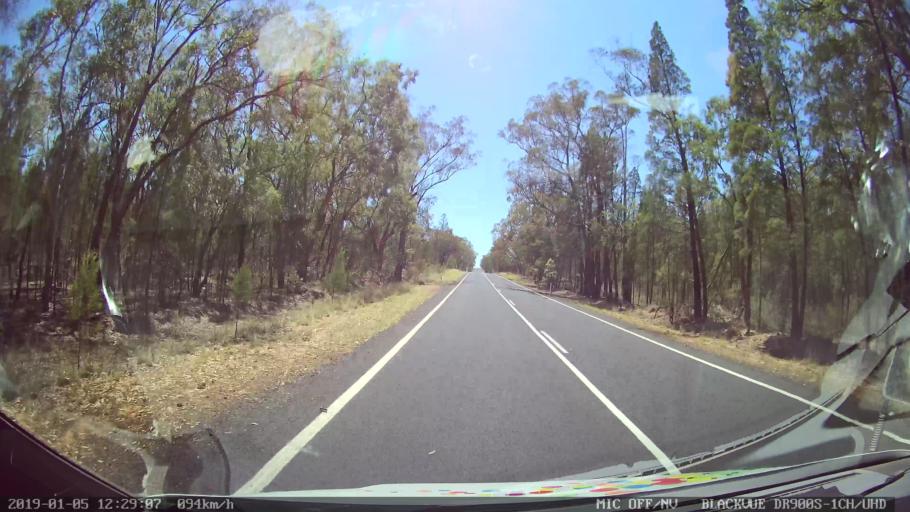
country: AU
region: New South Wales
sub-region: Warrumbungle Shire
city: Coonabarabran
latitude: -31.2354
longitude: 149.3328
